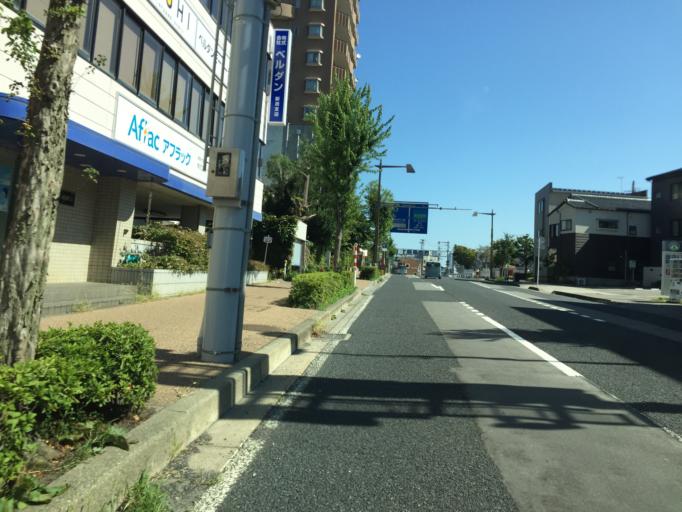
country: JP
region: Niigata
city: Niigata-shi
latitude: 37.9086
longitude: 139.0171
